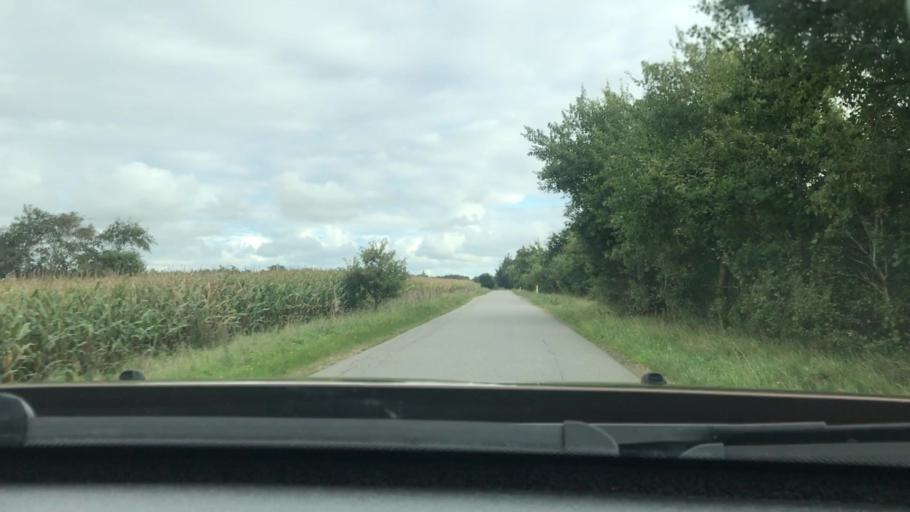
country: DK
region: South Denmark
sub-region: Esbjerg Kommune
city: Ribe
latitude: 55.3010
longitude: 8.7209
